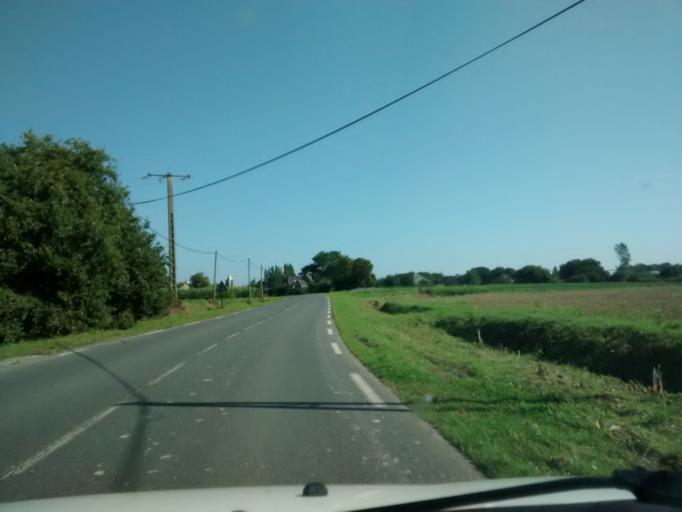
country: FR
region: Brittany
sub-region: Departement des Cotes-d'Armor
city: Pleumeur-Gautier
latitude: 48.8248
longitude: -3.1867
